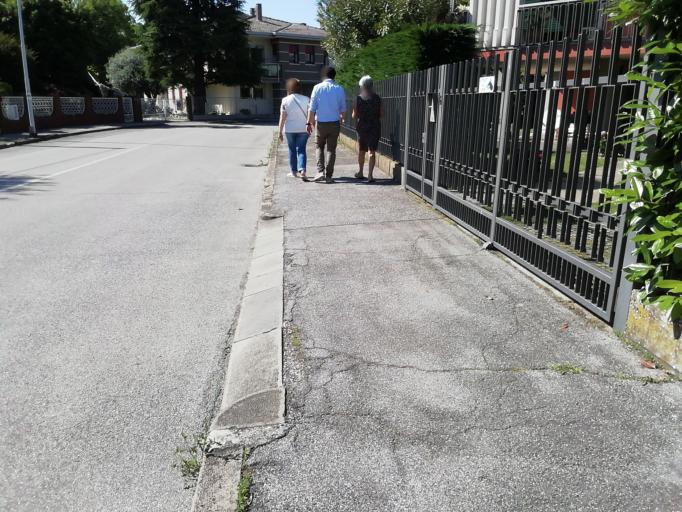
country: IT
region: Veneto
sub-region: Provincia di Padova
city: Padova
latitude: 45.4168
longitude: 11.9126
